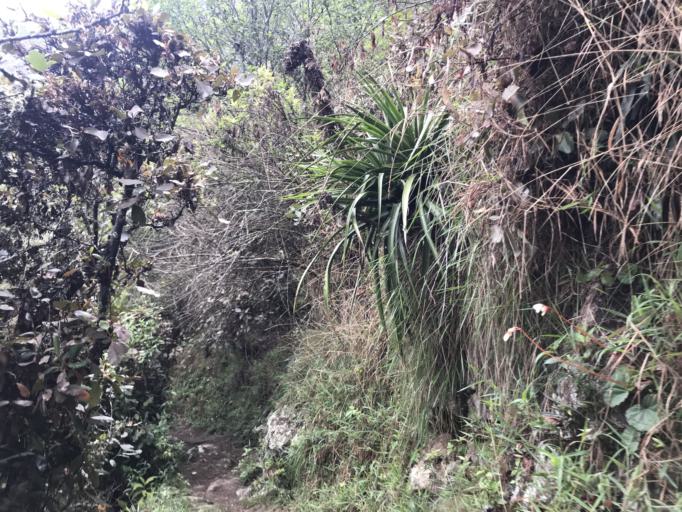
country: PE
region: Cusco
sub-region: Provincia de La Convencion
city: Santa Teresa
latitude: -13.1877
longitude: -72.5166
